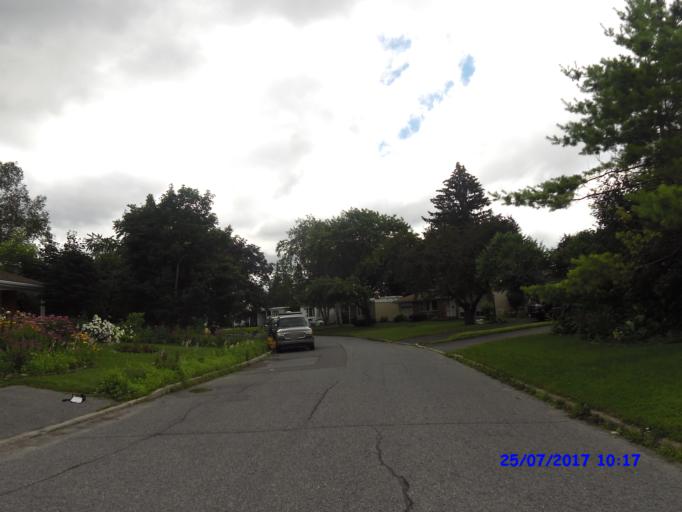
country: CA
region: Ontario
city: Ottawa
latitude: 45.3585
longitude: -75.7196
